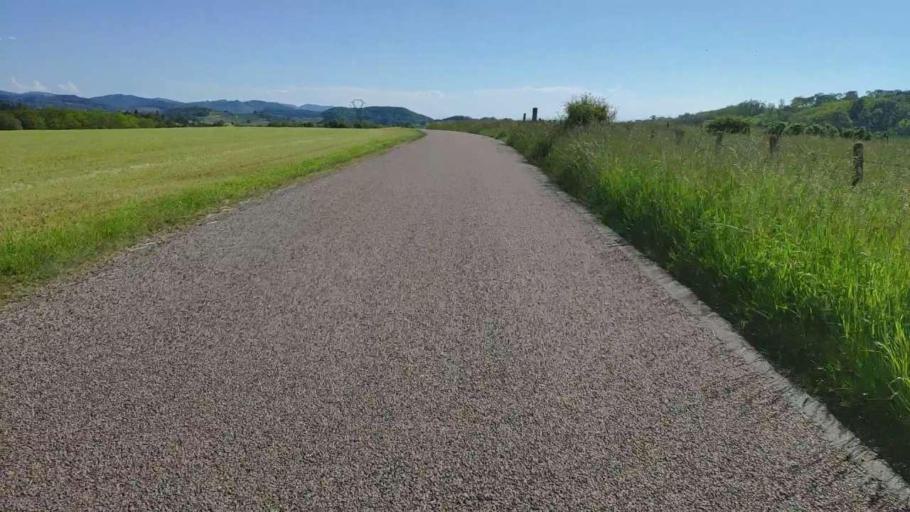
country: FR
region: Franche-Comte
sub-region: Departement du Jura
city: Perrigny
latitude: 46.7169
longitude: 5.5683
